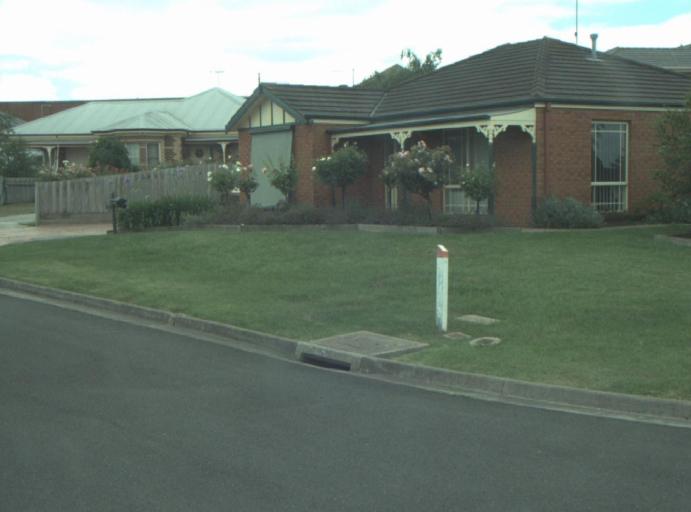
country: AU
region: Victoria
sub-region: Greater Geelong
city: Wandana Heights
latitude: -38.1877
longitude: 144.3110
